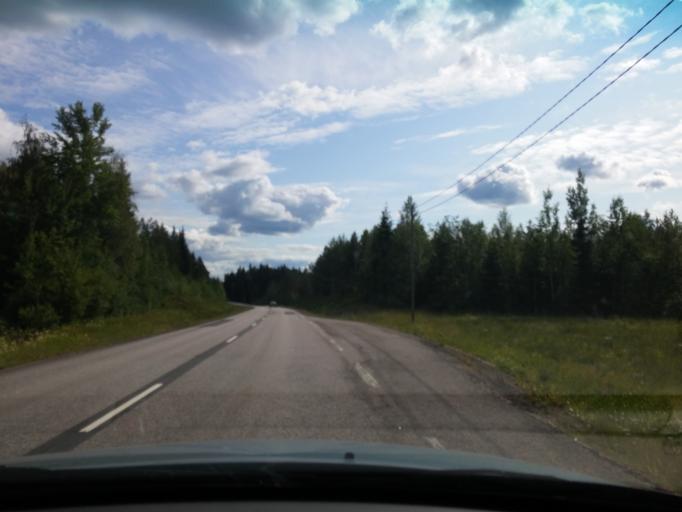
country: FI
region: Central Finland
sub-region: Keuruu
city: Multia
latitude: 62.3528
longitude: 24.7380
